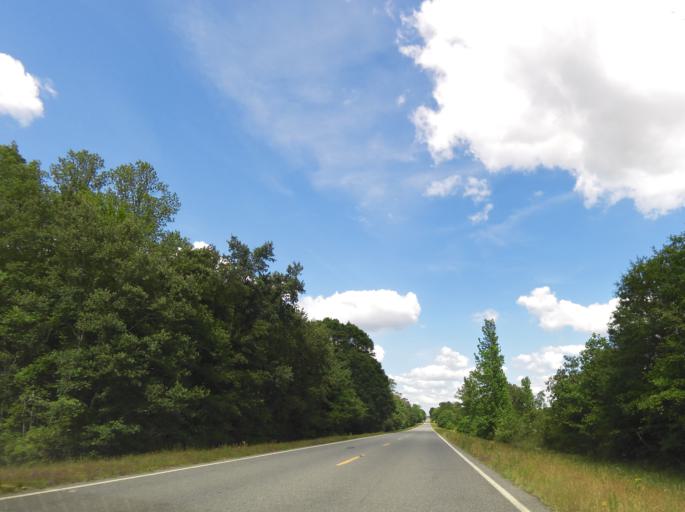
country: US
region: Georgia
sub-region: Telfair County
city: Helena
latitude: 32.2269
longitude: -82.9903
